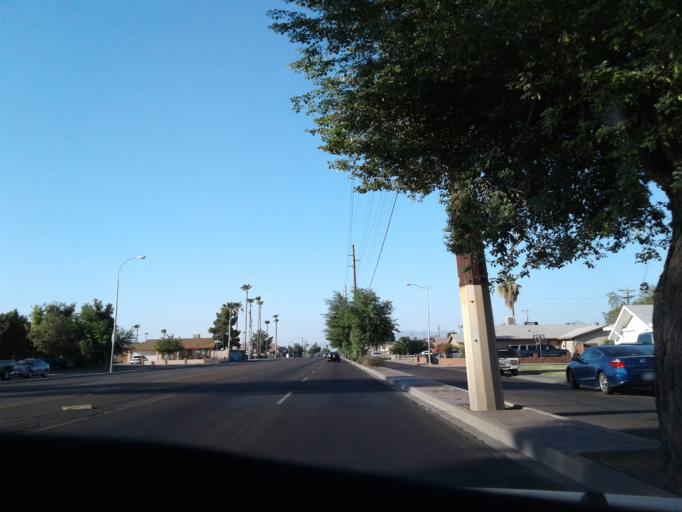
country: US
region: Arizona
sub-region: Maricopa County
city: Glendale
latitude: 33.4836
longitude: -112.1865
